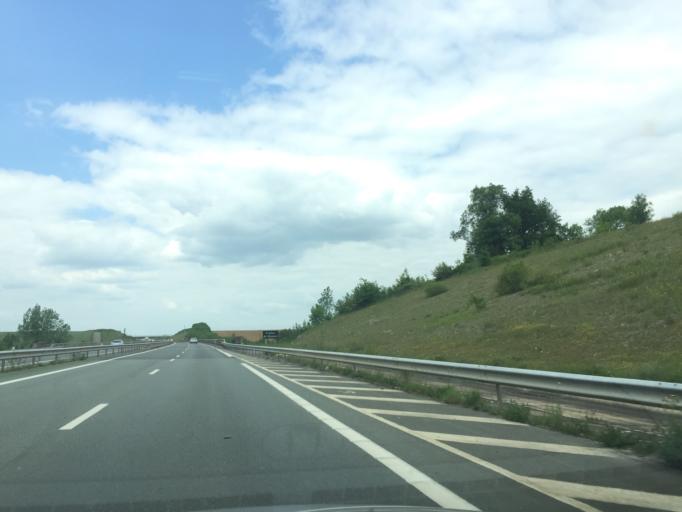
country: FR
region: Poitou-Charentes
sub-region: Departement des Deux-Sevres
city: Chauray
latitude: 46.3814
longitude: -0.3640
